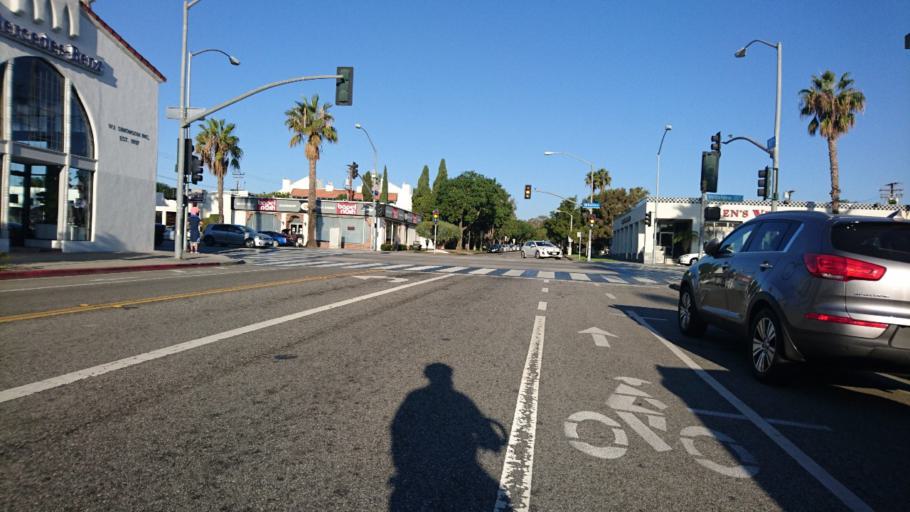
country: US
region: California
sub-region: Los Angeles County
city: Santa Monica
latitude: 34.0289
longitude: -118.4857
